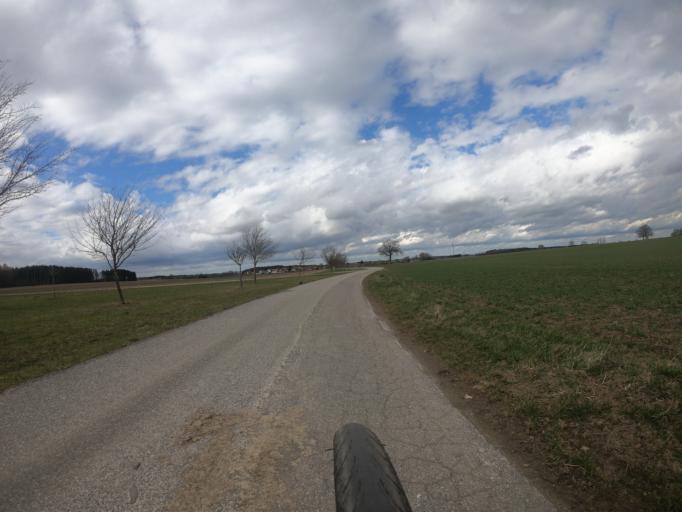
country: DE
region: Bavaria
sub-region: Upper Bavaria
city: Landsberied
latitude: 48.1725
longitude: 11.1967
